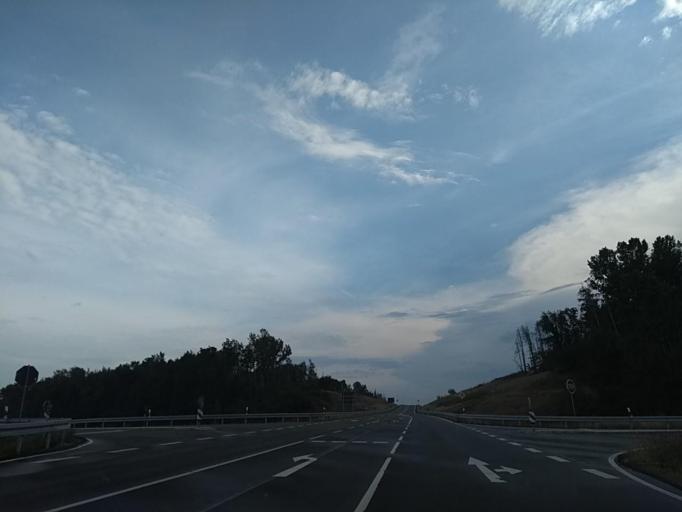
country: DE
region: Saxony-Anhalt
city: Muschwitz
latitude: 51.1837
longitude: 12.1273
